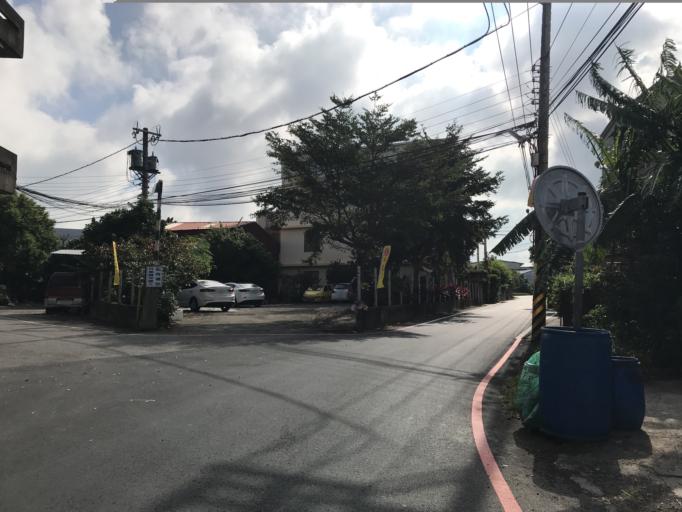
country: TW
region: Taiwan
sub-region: Hsinchu
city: Zhubei
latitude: 24.8101
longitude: 121.0036
